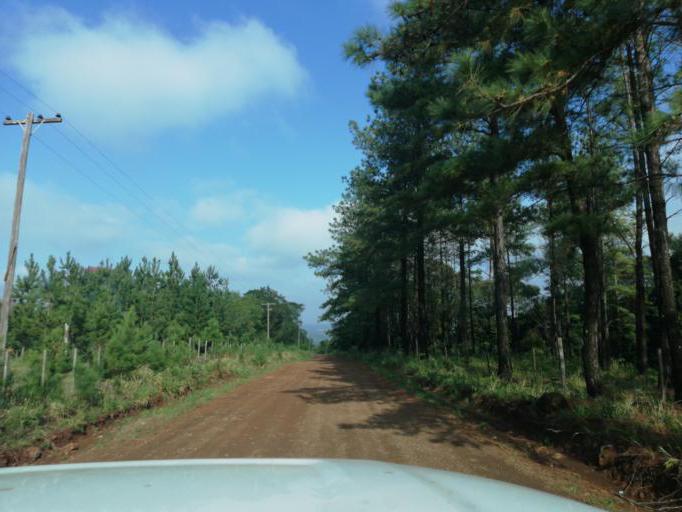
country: AR
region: Misiones
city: Cerro Azul
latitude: -27.5781
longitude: -55.5102
